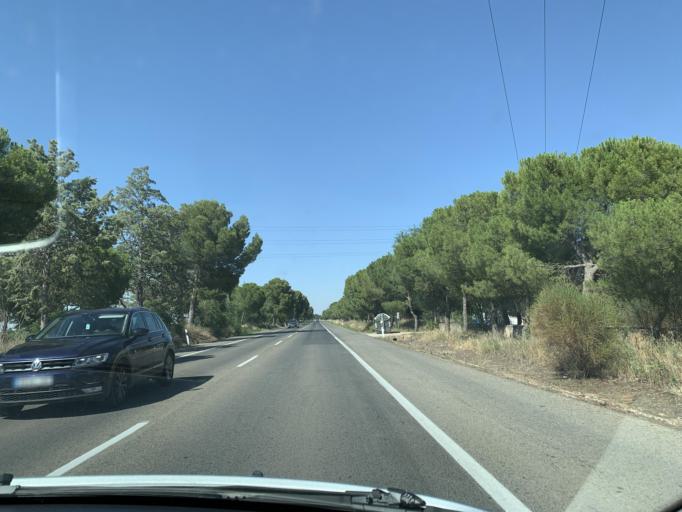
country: ES
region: Castille-La Mancha
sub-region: Provincia de Ciudad Real
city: Argamasilla de Alba
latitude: 39.1386
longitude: -3.0725
